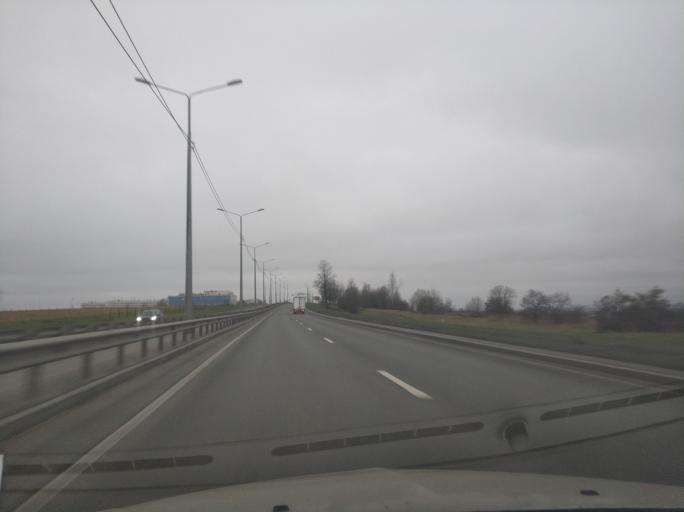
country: RU
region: St.-Petersburg
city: Pushkin
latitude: 59.7577
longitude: 30.3774
